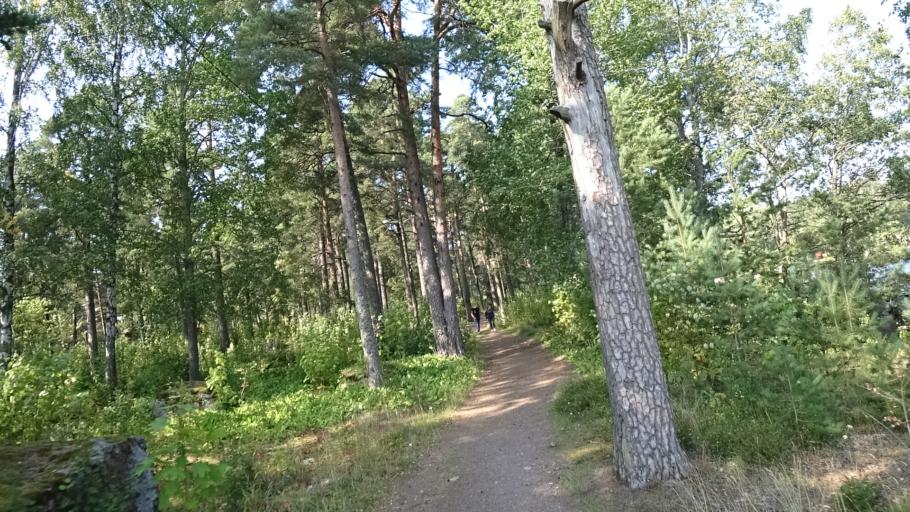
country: FI
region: Kymenlaakso
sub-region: Kotka-Hamina
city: Kotka
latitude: 60.4499
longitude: 26.9461
